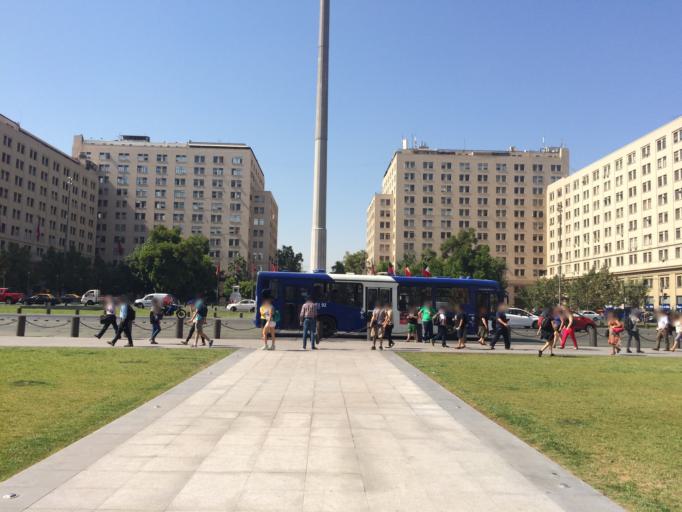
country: CL
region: Santiago Metropolitan
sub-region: Provincia de Santiago
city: Santiago
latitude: -33.4441
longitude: -70.6536
